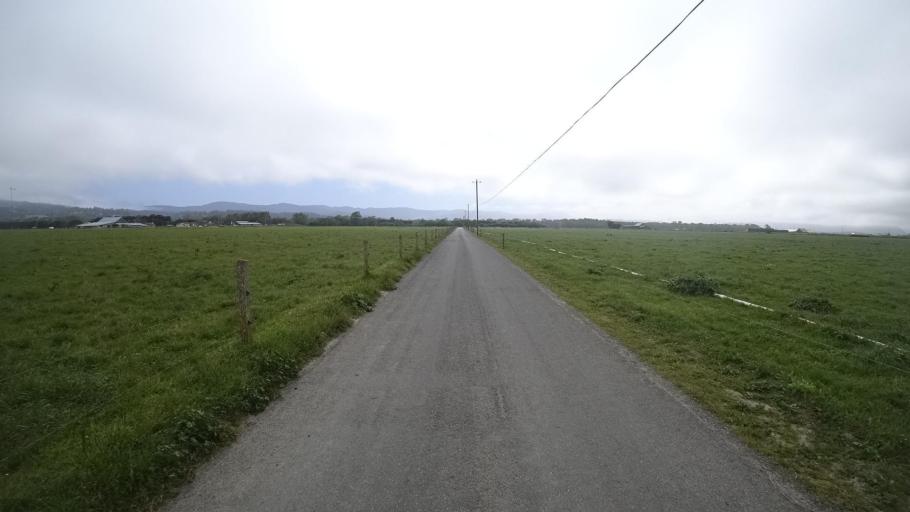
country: US
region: California
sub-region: Humboldt County
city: Fortuna
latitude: 40.5917
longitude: -124.1970
